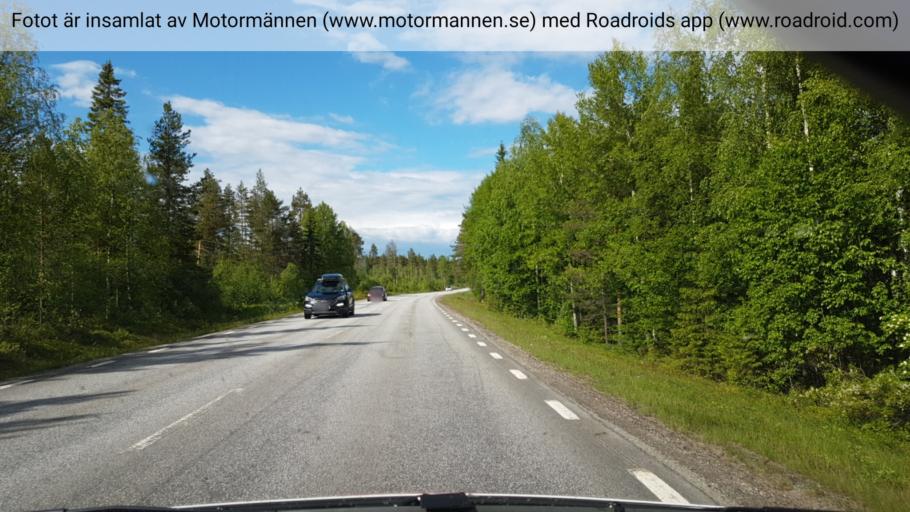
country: SE
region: Norrbotten
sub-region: Overkalix Kommun
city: OEverkalix
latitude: 66.2732
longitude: 22.8184
